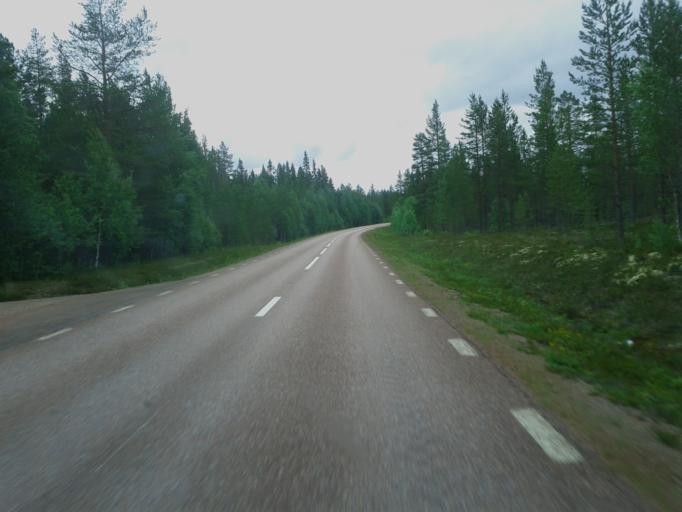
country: NO
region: Hedmark
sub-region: Trysil
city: Innbygda
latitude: 61.7051
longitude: 13.0214
